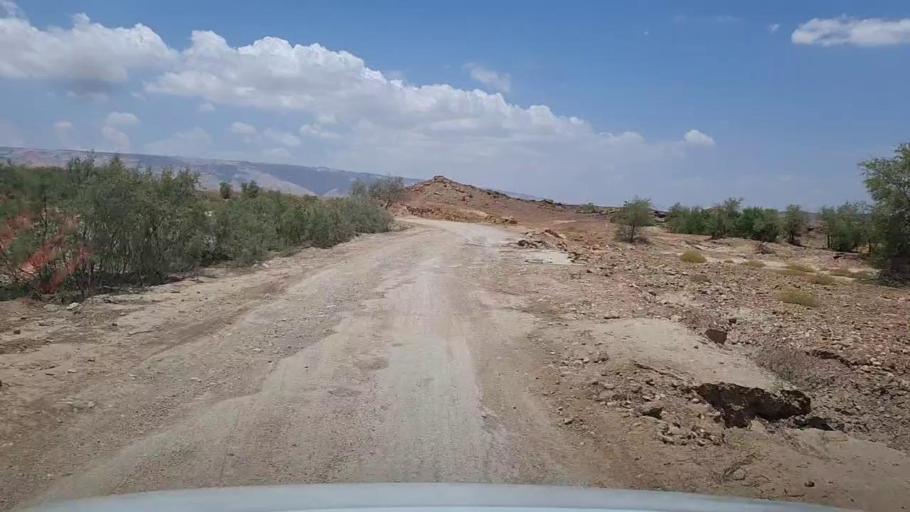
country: PK
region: Sindh
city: Bhan
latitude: 26.3171
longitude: 67.5773
